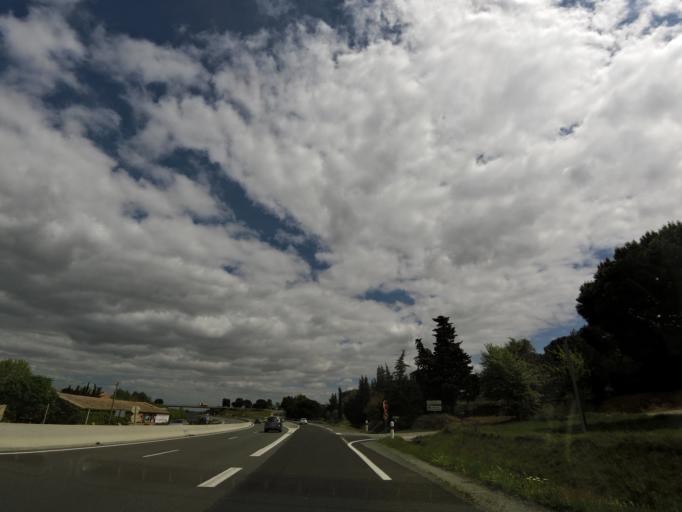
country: FR
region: Languedoc-Roussillon
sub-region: Departement de l'Aude
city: Trebes
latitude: 43.2043
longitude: 2.4115
